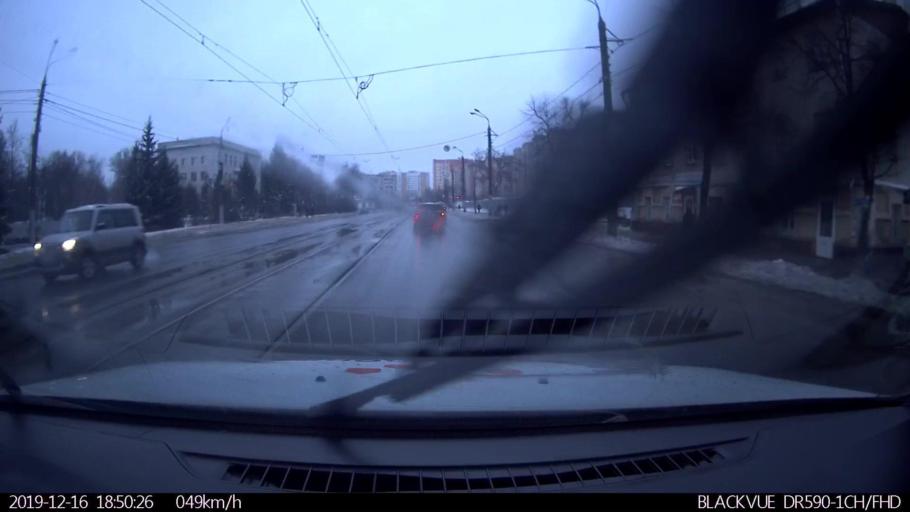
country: RU
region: Nizjnij Novgorod
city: Nizhniy Novgorod
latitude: 56.3100
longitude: 43.9369
